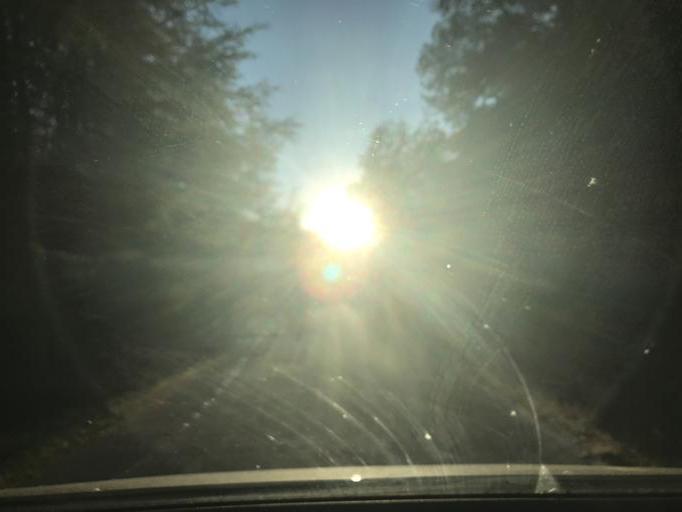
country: ES
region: Andalusia
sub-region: Provincia de Granada
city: Beas de Granada
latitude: 37.2915
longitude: -3.4884
